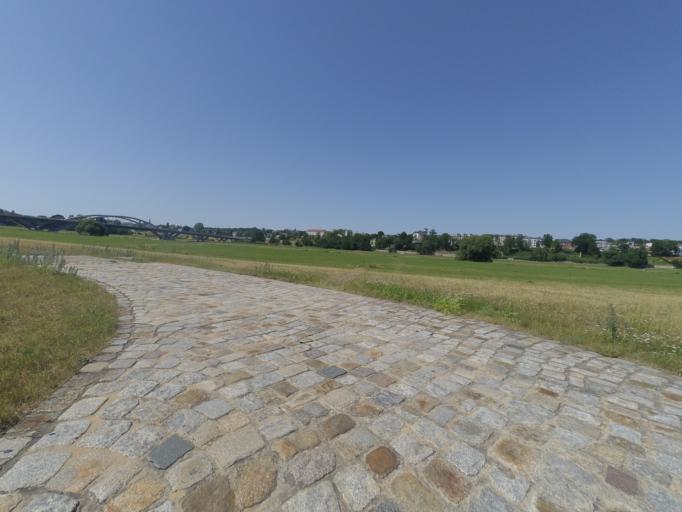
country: DE
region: Saxony
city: Albertstadt
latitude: 51.0615
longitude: 13.7815
